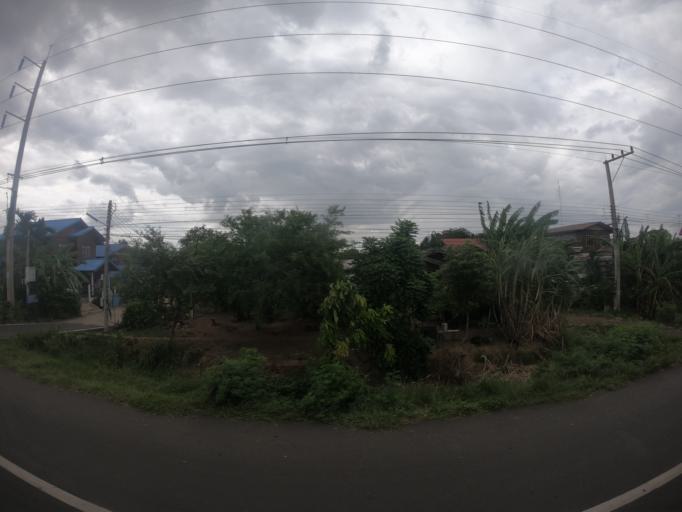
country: TH
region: Buriram
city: Chaloem Phra Kiat
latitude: 14.6097
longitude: 102.9212
